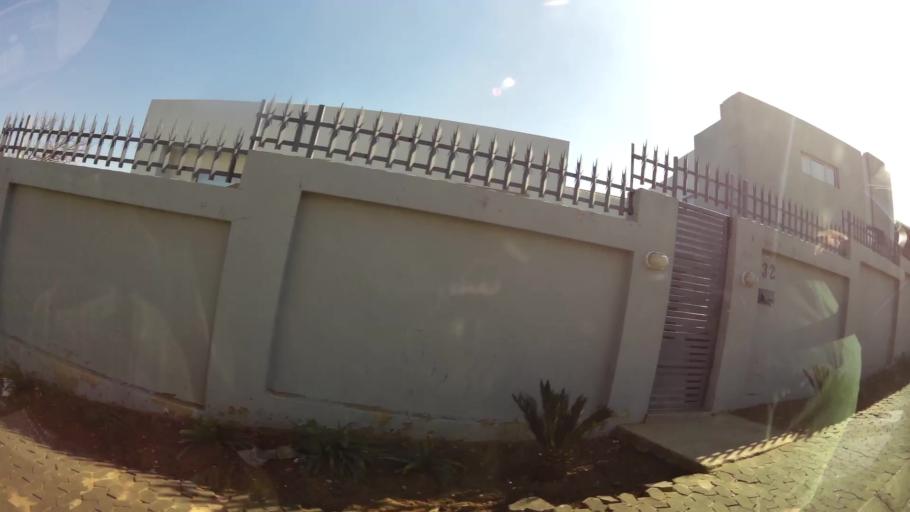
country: ZA
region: Gauteng
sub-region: City of Johannesburg Metropolitan Municipality
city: Johannesburg
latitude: -26.1913
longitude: 27.9641
